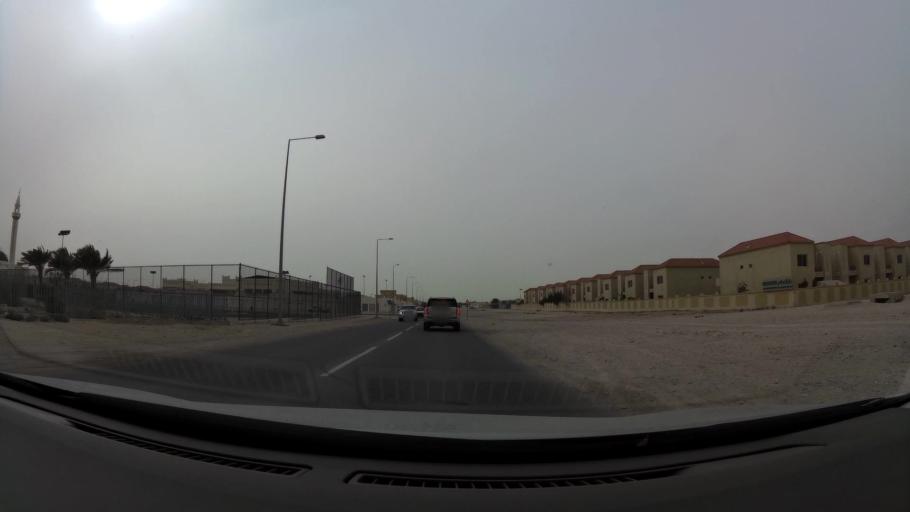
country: QA
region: Baladiyat ad Dawhah
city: Doha
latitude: 25.2422
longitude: 51.5121
